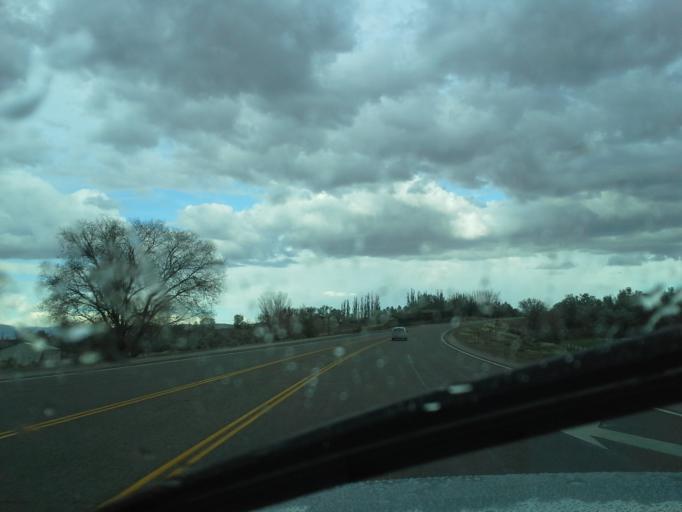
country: US
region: Wyoming
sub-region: Big Horn County
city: Lovell
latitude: 44.8363
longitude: -108.3775
